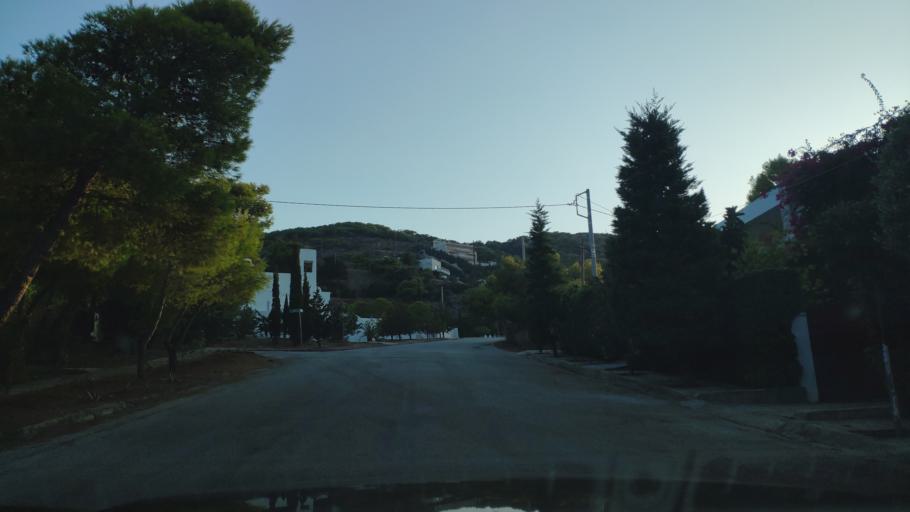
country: GR
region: Attica
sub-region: Nomarchia Anatolikis Attikis
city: Limin Mesoyaias
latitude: 37.9175
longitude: 24.0225
